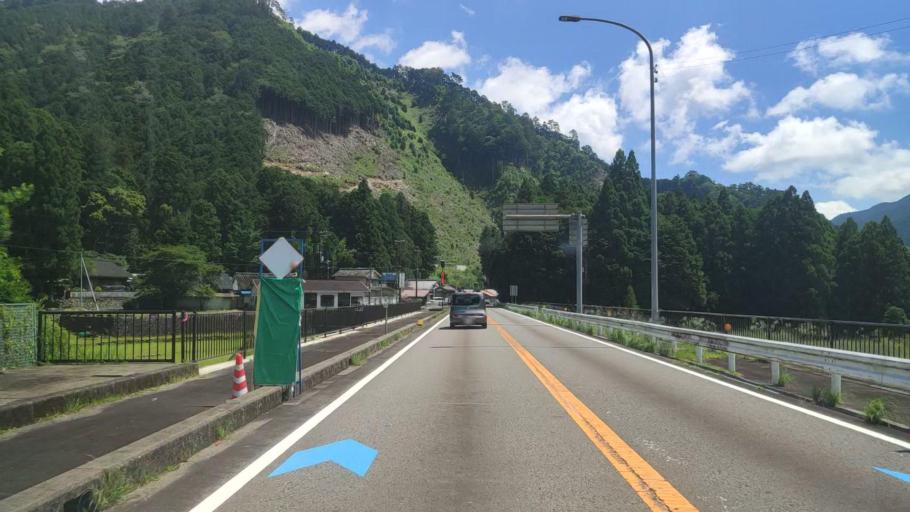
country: JP
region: Mie
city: Owase
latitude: 33.9853
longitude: 136.1082
